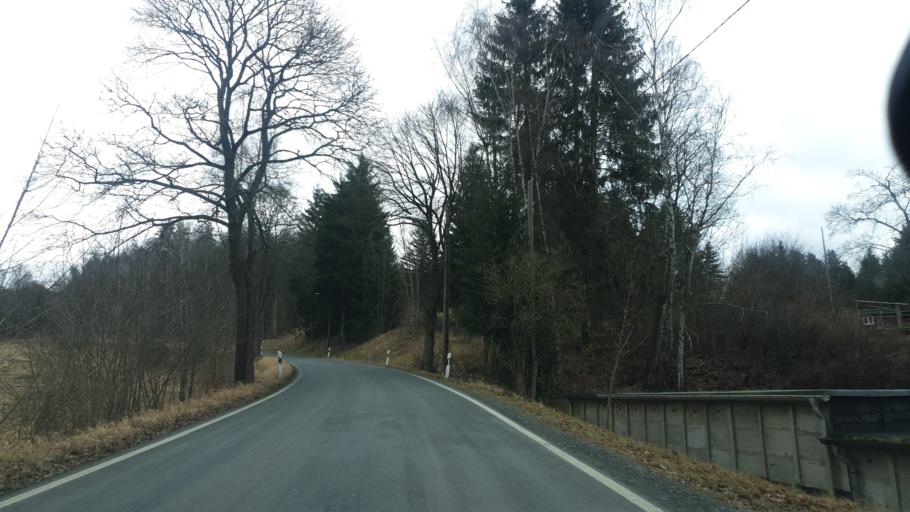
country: DE
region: Saxony
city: Bad Elster
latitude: 50.2745
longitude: 12.2533
